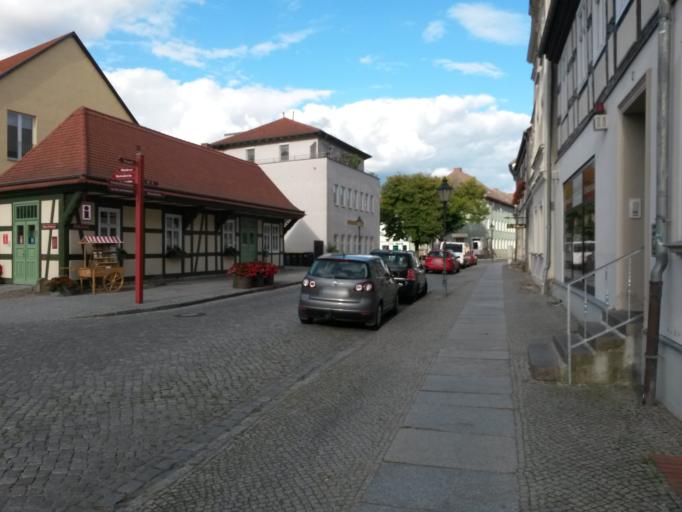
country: DE
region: Brandenburg
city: Angermunde
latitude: 53.0172
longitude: 14.0033
